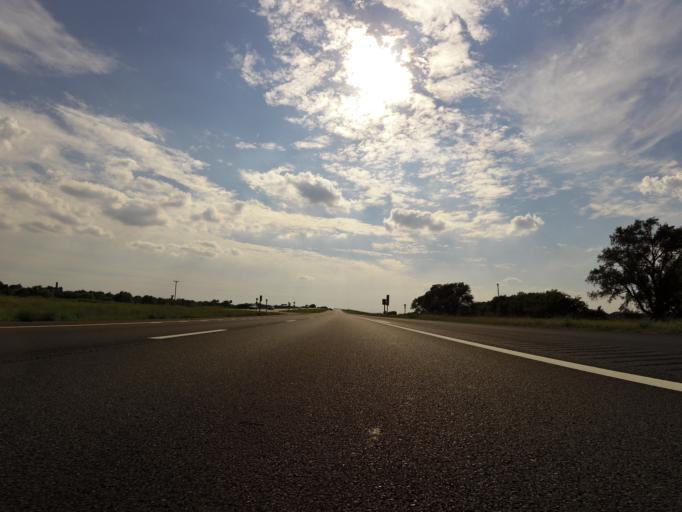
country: US
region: Kansas
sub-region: Reno County
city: Haven
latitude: 37.8759
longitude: -97.6823
